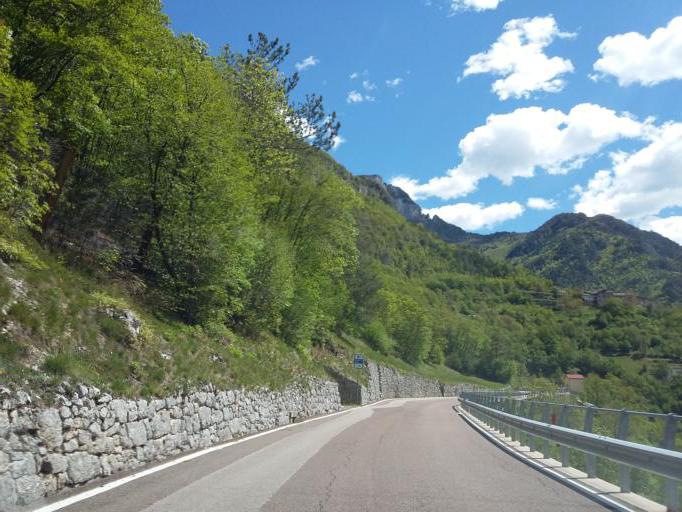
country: IT
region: Trentino-Alto Adige
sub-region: Provincia di Trento
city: Moscheri
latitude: 45.8240
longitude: 11.0872
